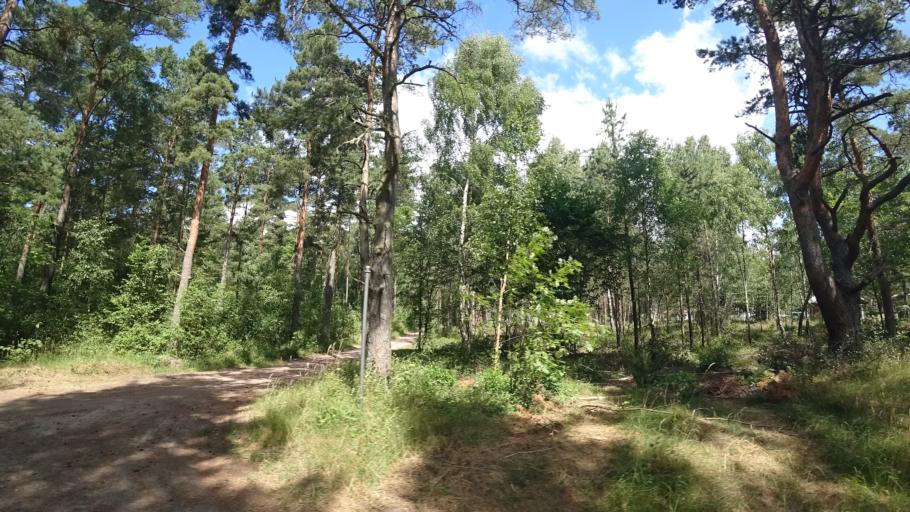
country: SE
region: Skane
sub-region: Kristianstads Kommun
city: Ahus
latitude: 55.9595
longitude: 14.2851
